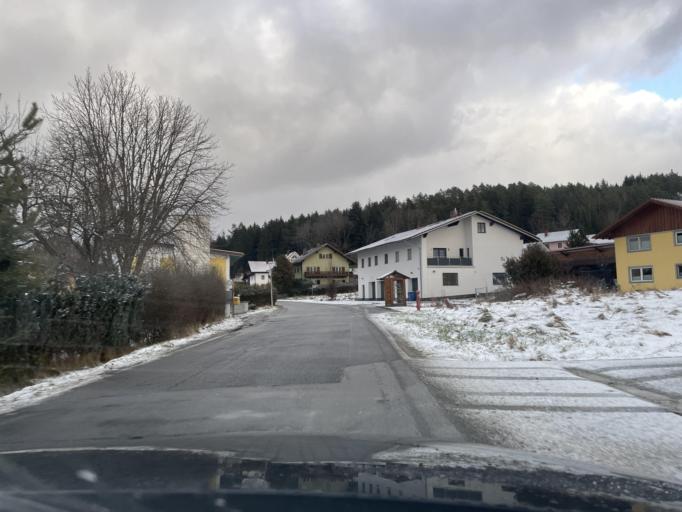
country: DE
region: Bavaria
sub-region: Lower Bavaria
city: Prackenbach
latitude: 49.1047
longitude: 12.8445
